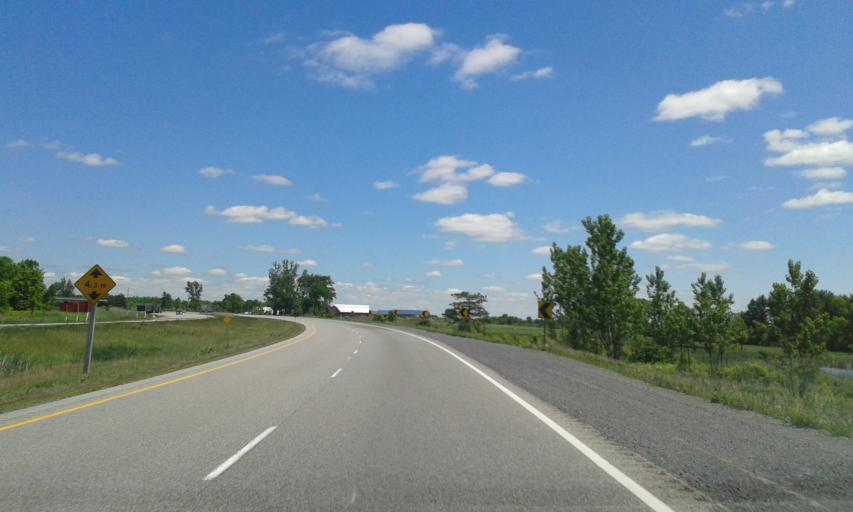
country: US
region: New York
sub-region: St. Lawrence County
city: Norfolk
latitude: 44.9625
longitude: -75.0861
